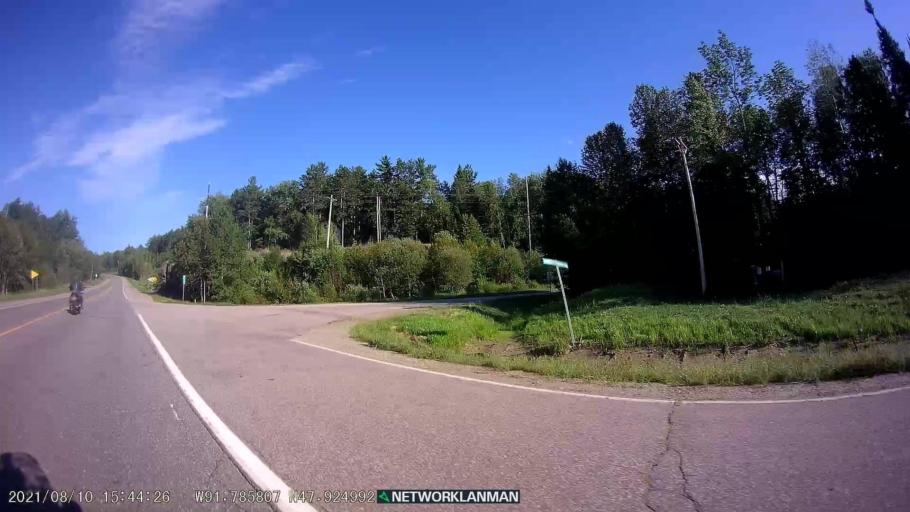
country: US
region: Minnesota
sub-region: Saint Louis County
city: Ely
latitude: 47.9249
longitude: -91.7854
